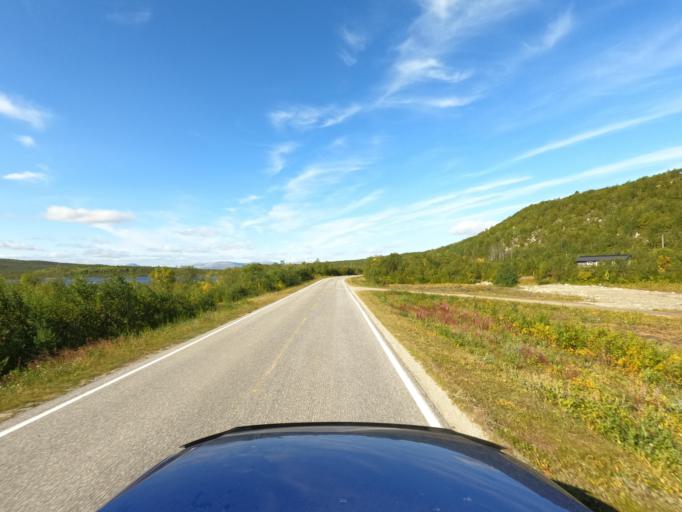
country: NO
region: Finnmark Fylke
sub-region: Porsanger
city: Lakselv
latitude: 69.7587
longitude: 25.2082
